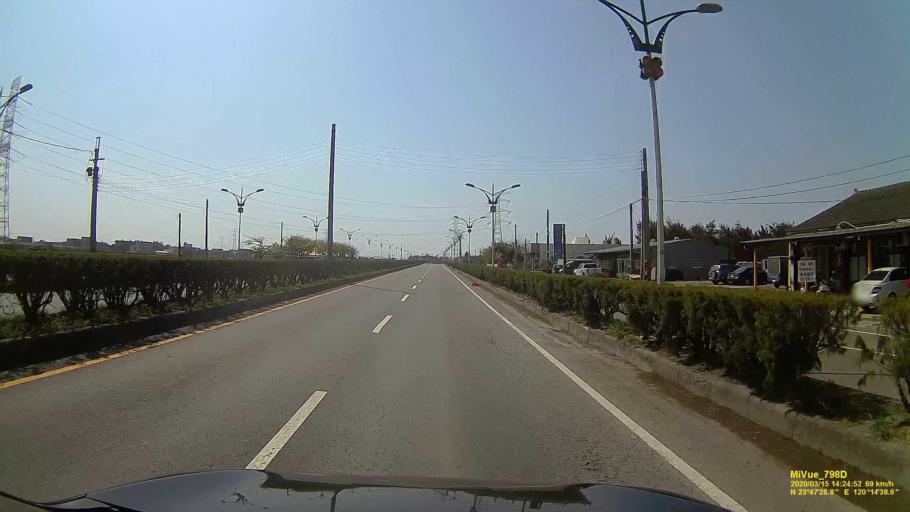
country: TW
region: Taiwan
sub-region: Yunlin
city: Douliu
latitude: 23.7914
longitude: 120.2438
